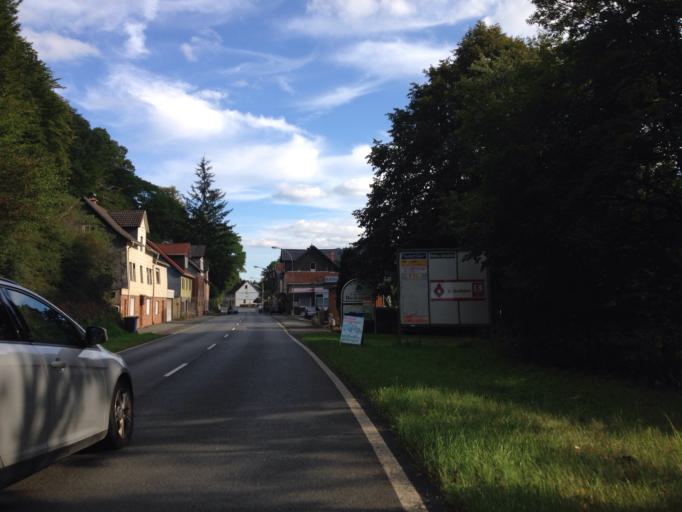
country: DE
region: Hesse
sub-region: Regierungsbezirk Giessen
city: Biedenkopf
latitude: 50.9228
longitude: 8.5034
